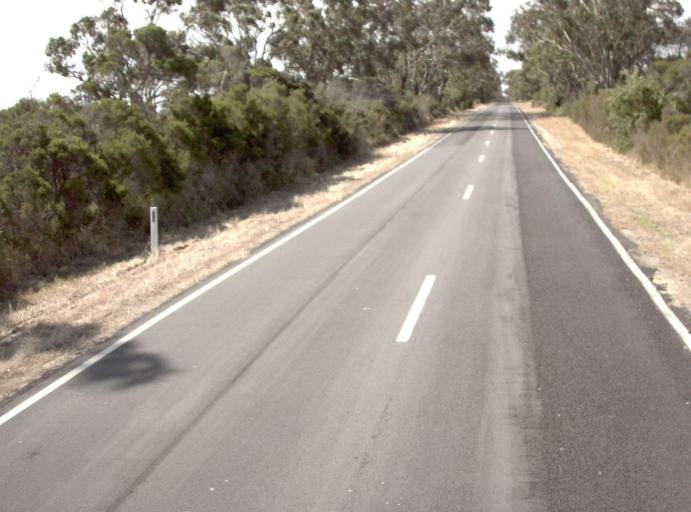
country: AU
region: Victoria
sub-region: Wellington
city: Sale
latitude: -38.3161
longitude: 147.1556
